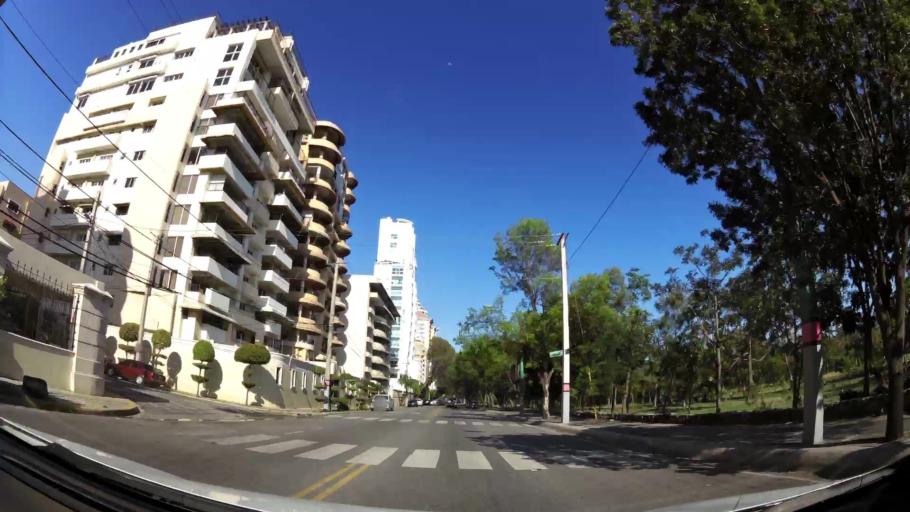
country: DO
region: Nacional
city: Bella Vista
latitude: 18.4367
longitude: -69.9795
